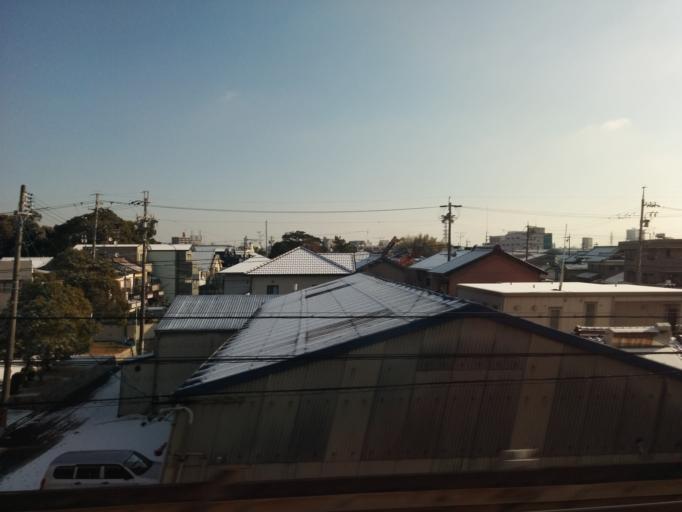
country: JP
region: Aichi
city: Obu
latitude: 35.0811
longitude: 136.9341
